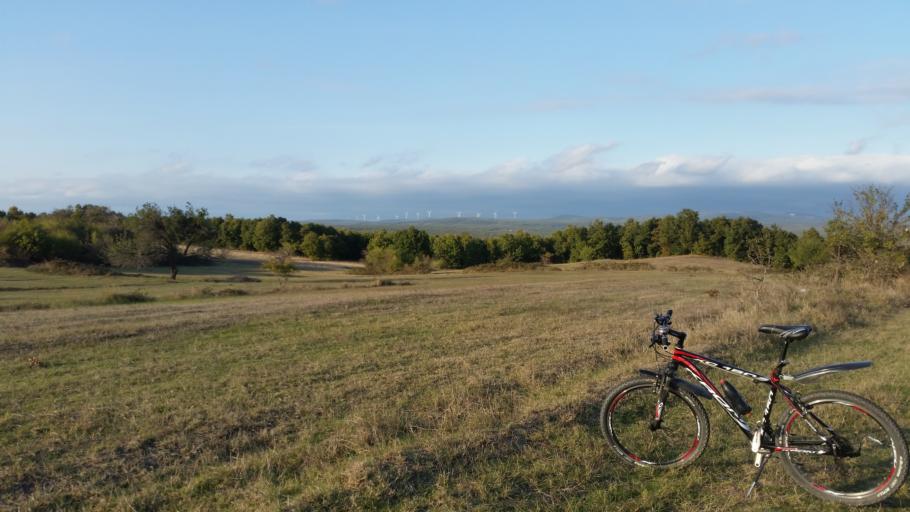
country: TR
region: Tekirdag
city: Saray
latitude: 41.3948
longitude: 28.0198
